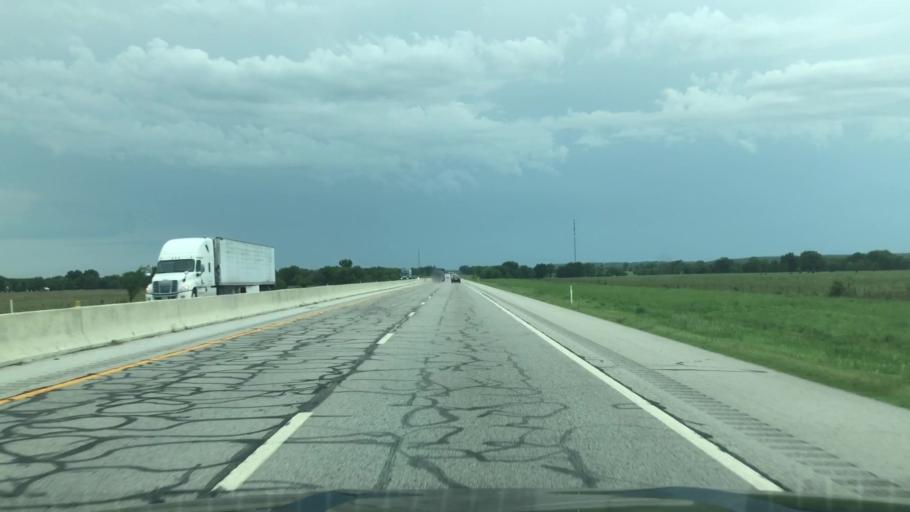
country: US
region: Oklahoma
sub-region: Craig County
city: Vinita
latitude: 36.5180
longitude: -95.2622
